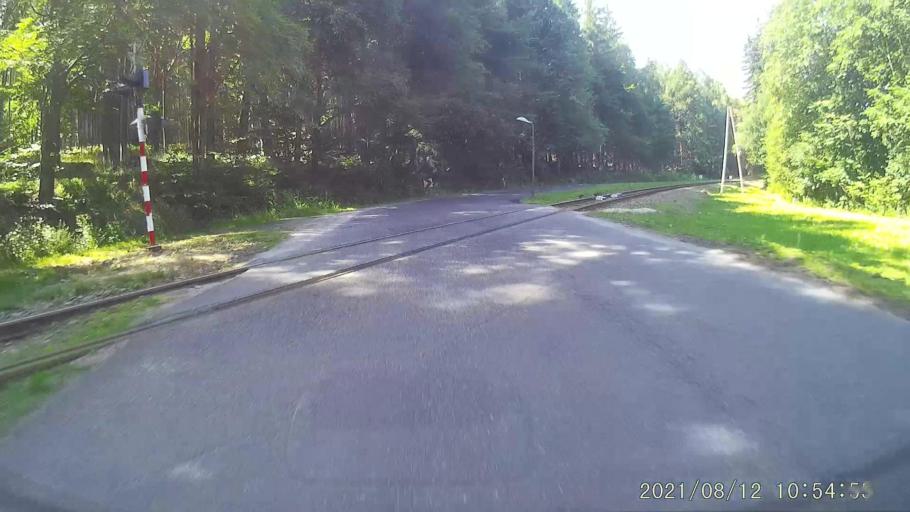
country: PL
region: Lower Silesian Voivodeship
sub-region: Powiat klodzki
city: Szczytna
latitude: 50.4027
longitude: 16.4709
